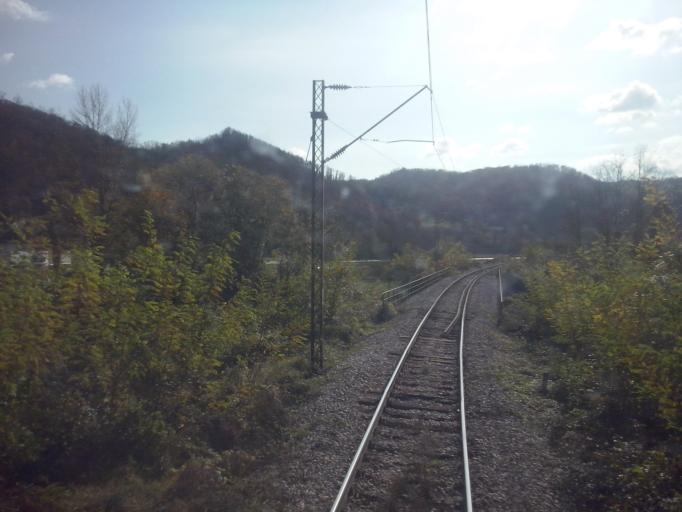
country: RS
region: Central Serbia
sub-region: Zlatiborski Okrug
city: Pozega
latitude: 43.9093
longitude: 20.0013
